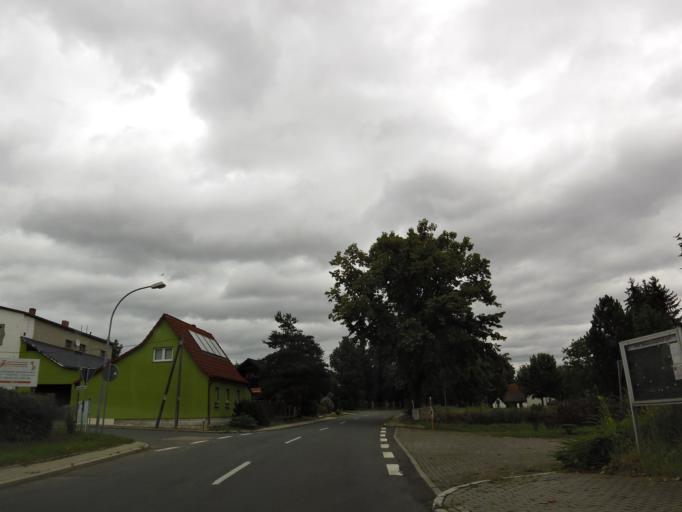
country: DE
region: Saxony-Anhalt
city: Teuchern
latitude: 51.1274
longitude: 12.0389
